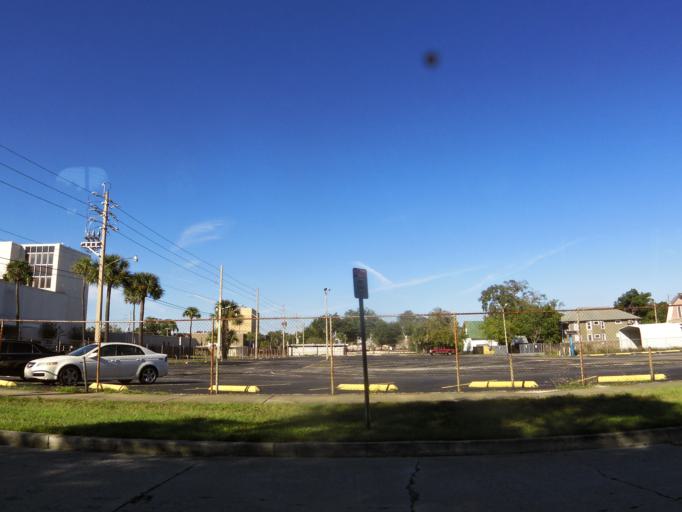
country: US
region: Florida
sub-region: Duval County
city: Jacksonville
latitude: 30.3477
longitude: -81.6609
